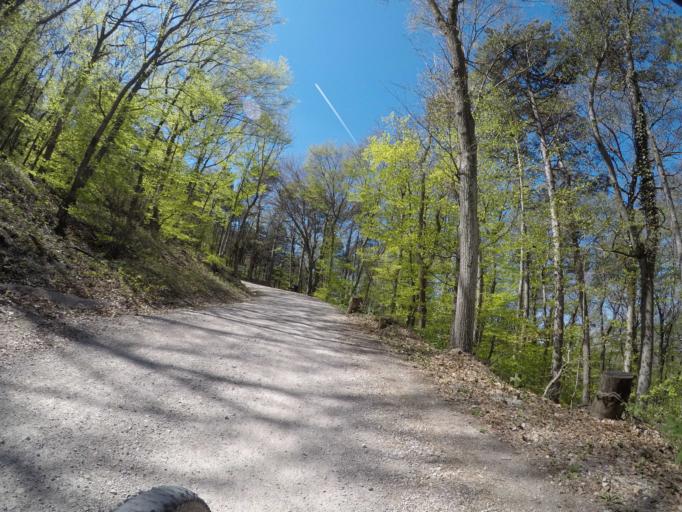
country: AT
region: Lower Austria
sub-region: Politischer Bezirk Modling
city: Hinterbruehl
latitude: 48.0613
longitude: 16.2523
